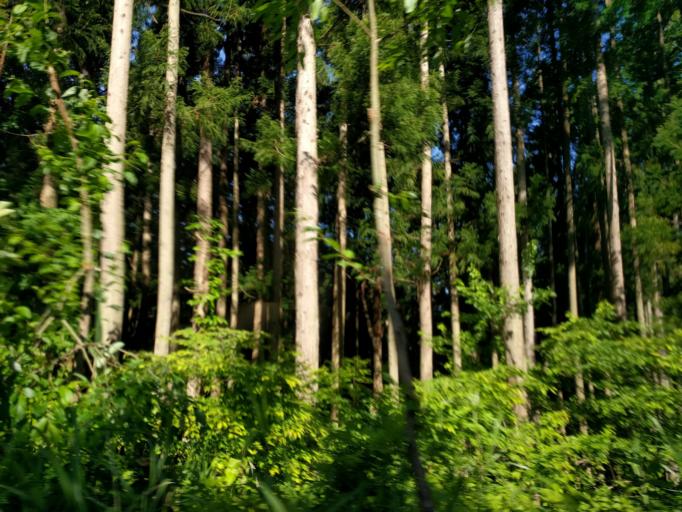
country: JP
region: Fukushima
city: Kitakata
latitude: 37.3867
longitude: 139.8289
